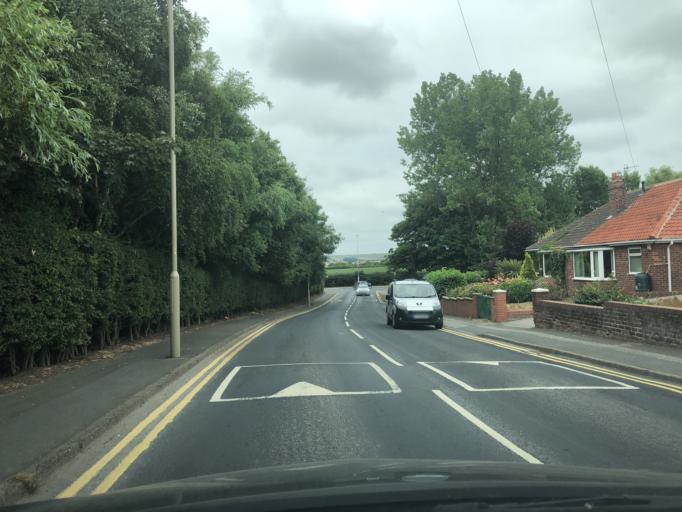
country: GB
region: England
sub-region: North Yorkshire
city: Scarborough
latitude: 54.2378
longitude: -0.3952
